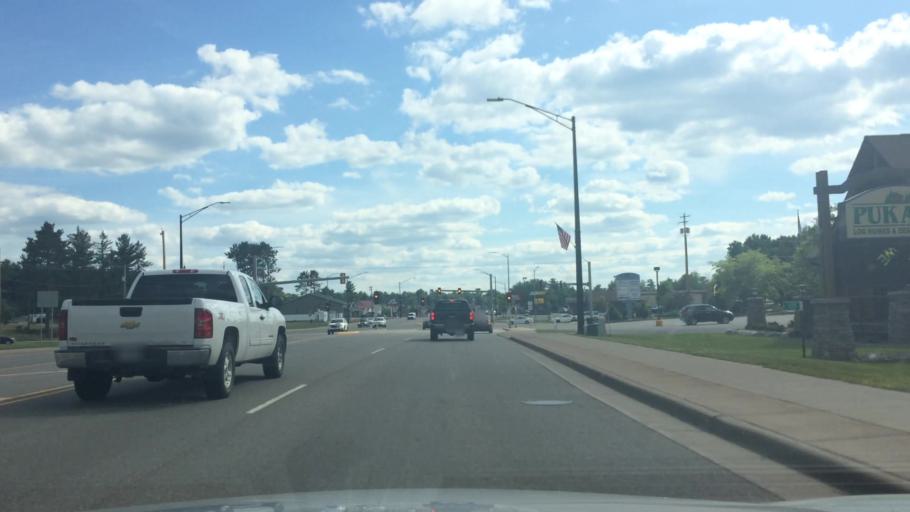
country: US
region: Wisconsin
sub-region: Vilas County
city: Lac du Flambeau
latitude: 45.8919
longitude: -89.7005
